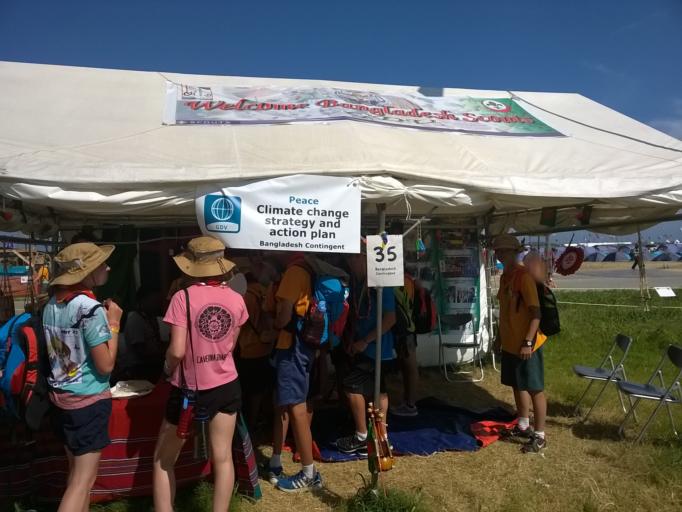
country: JP
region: Yamaguchi
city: Ogori-shimogo
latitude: 34.0152
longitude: 131.3710
